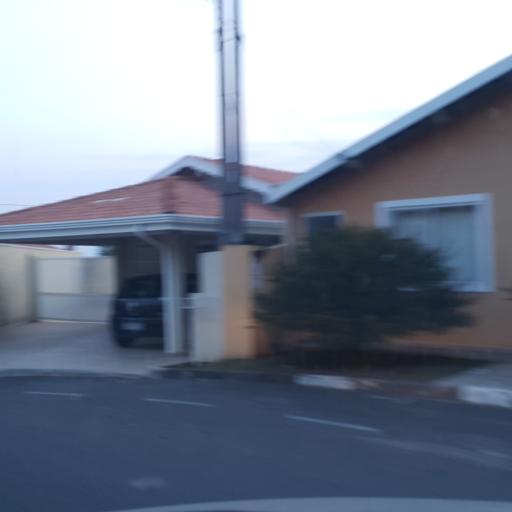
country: BR
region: Sao Paulo
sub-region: Louveira
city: Louveira
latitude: -23.0718
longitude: -46.9566
